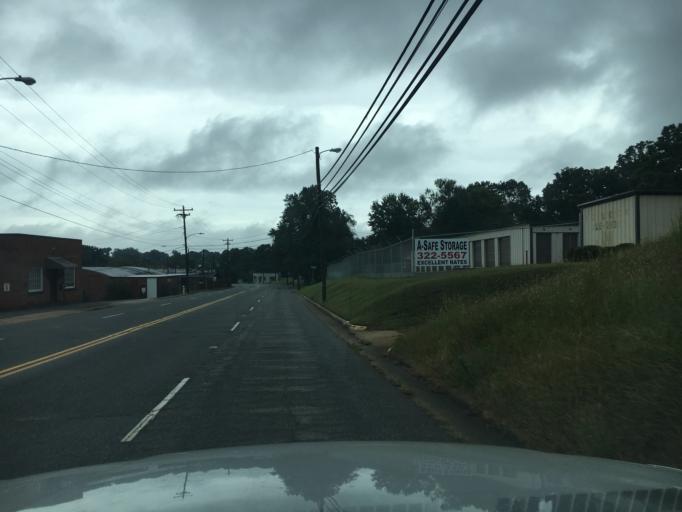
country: US
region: North Carolina
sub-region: Catawba County
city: Hickory
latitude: 35.7417
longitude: -81.3594
